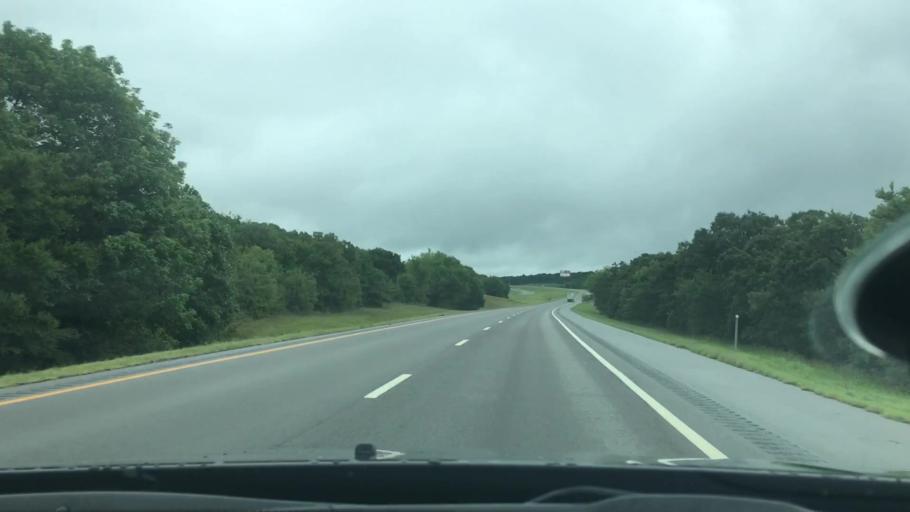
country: US
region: Oklahoma
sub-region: Okmulgee County
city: Henryetta
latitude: 35.4326
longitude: -95.8597
